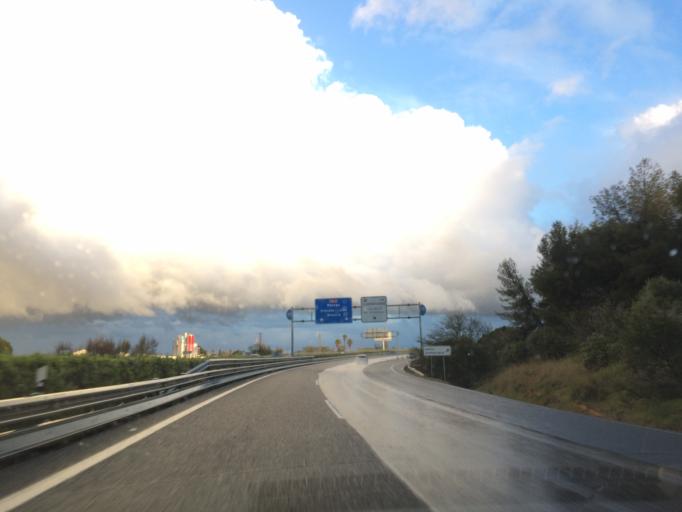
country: ES
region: Andalusia
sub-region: Provincia de Sevilla
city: Alcala de Guadaira
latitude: 37.3453
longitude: -5.8229
